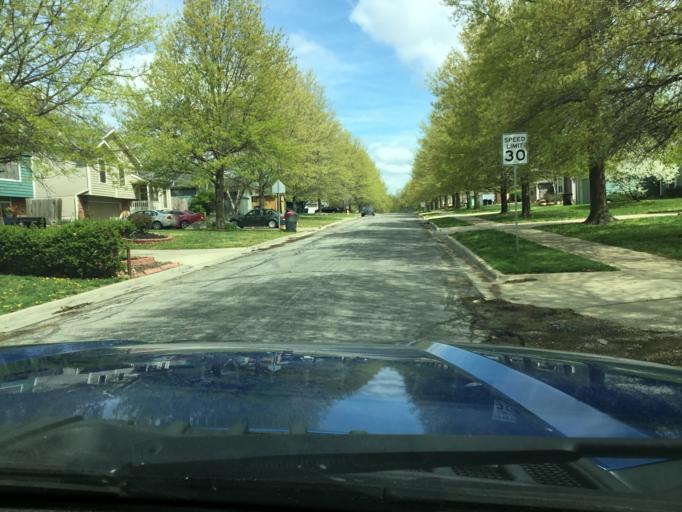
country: US
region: Kansas
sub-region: Douglas County
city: Lawrence
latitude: 38.9357
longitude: -95.2100
